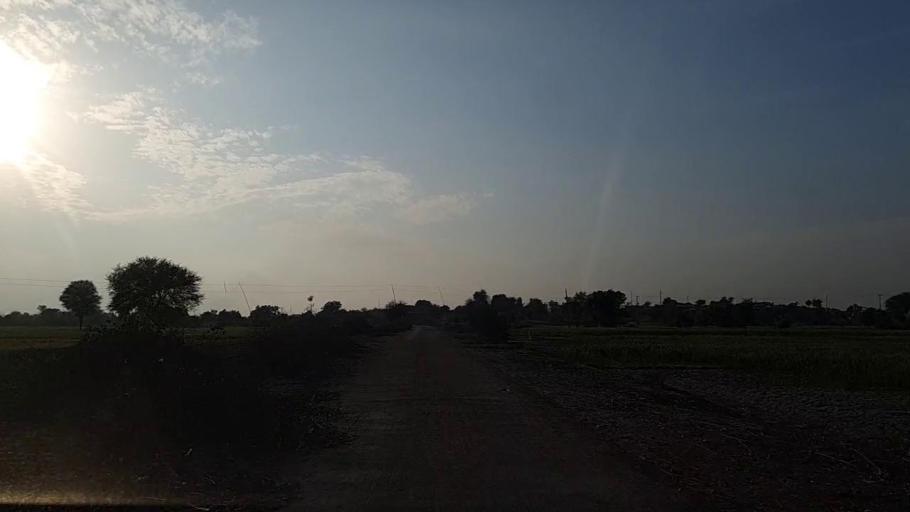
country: PK
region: Sindh
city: Jam Sahib
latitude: 26.3955
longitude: 68.5259
